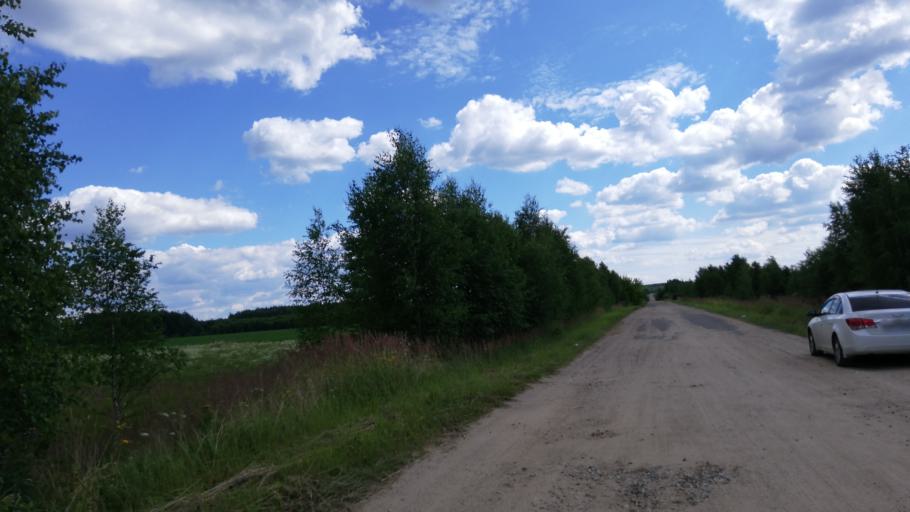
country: RU
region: Jaroslavl
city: Levashevo
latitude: 57.6380
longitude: 40.4622
